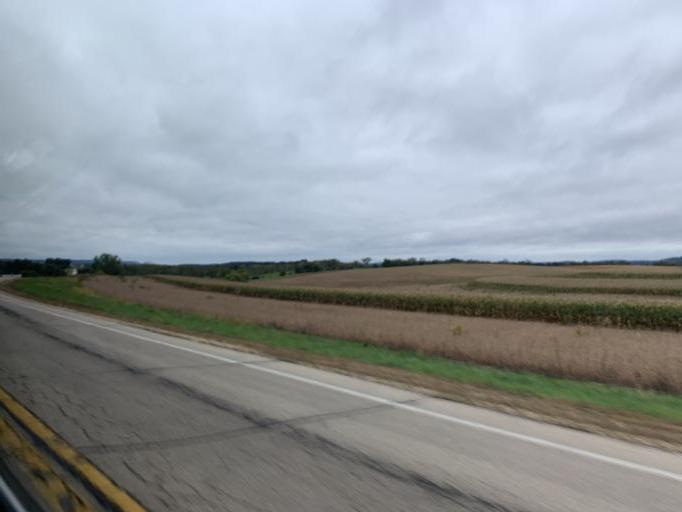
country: US
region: Wisconsin
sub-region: Grant County
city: Muscoda
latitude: 43.2196
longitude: -90.5587
